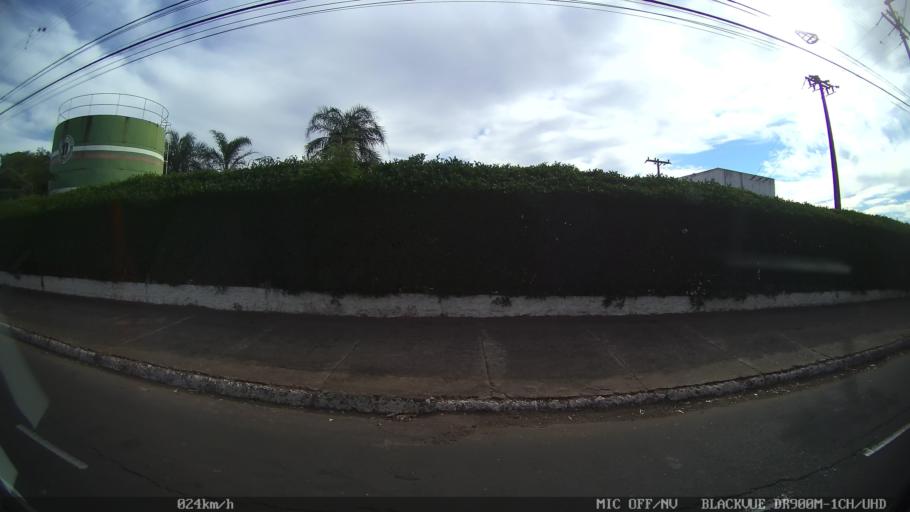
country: BR
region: Sao Paulo
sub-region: Catanduva
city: Catanduva
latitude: -21.1377
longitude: -48.9948
